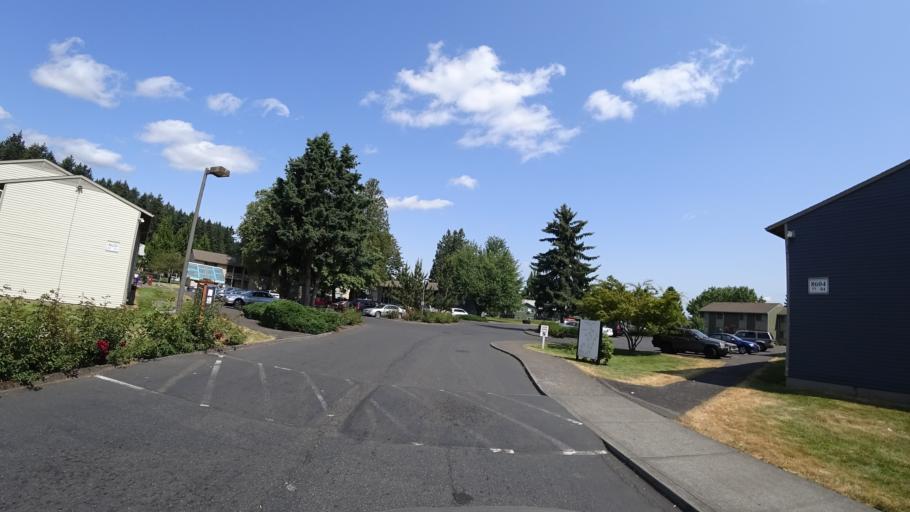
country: US
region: Oregon
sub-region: Washington County
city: West Haven
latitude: 45.6007
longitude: -122.7495
